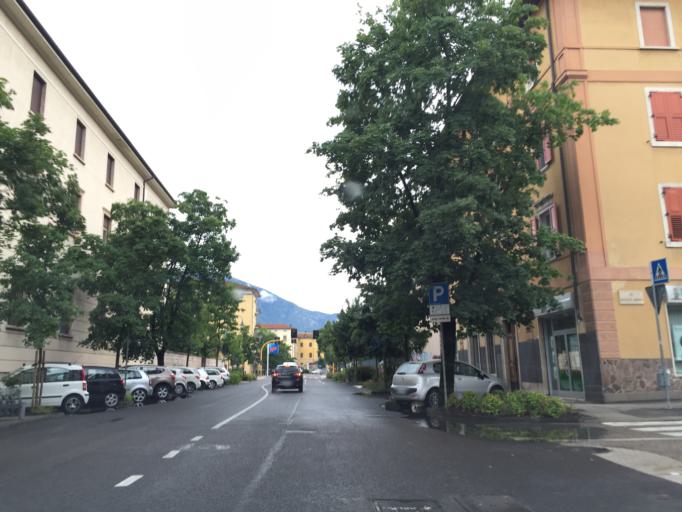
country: IT
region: Trentino-Alto Adige
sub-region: Provincia di Trento
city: Trento
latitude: 46.0653
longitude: 11.1193
